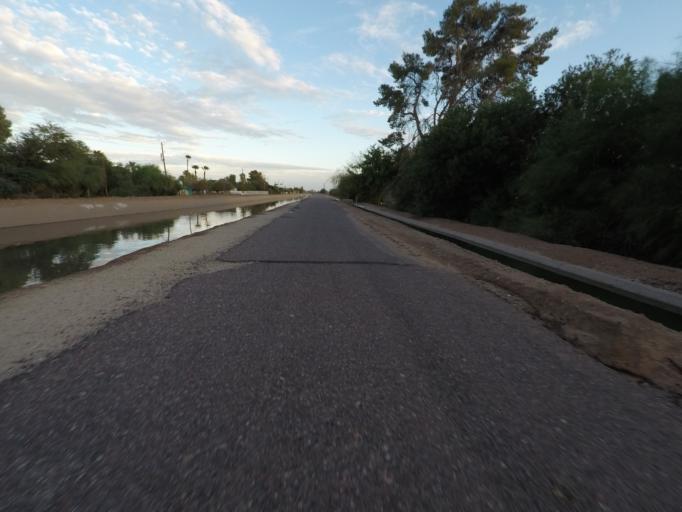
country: US
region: Arizona
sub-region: Maricopa County
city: Phoenix
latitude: 33.4719
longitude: -112.0241
